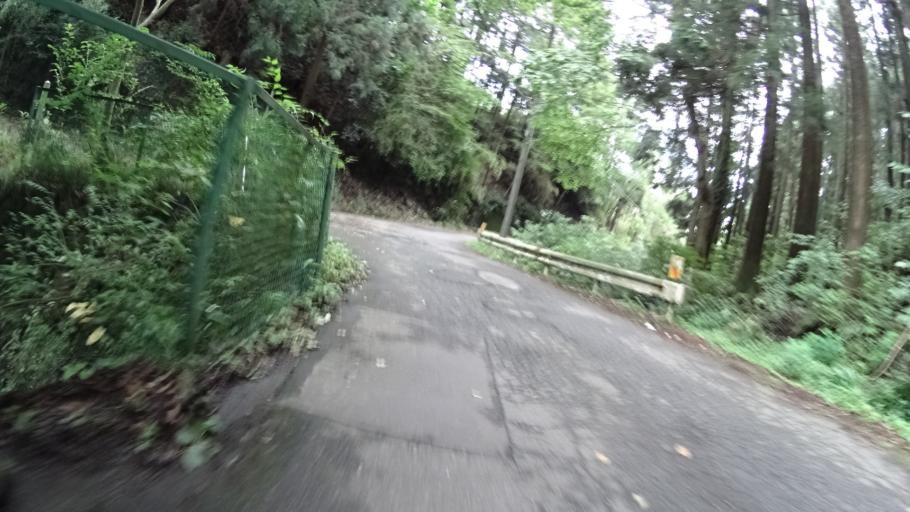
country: JP
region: Kanagawa
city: Atsugi
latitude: 35.4984
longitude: 139.2663
